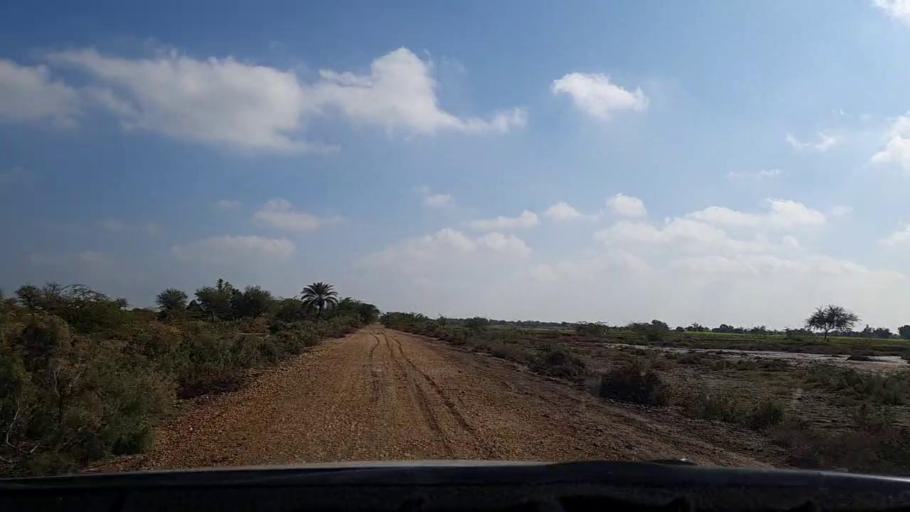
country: PK
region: Sindh
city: Pithoro
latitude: 25.7232
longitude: 69.2927
